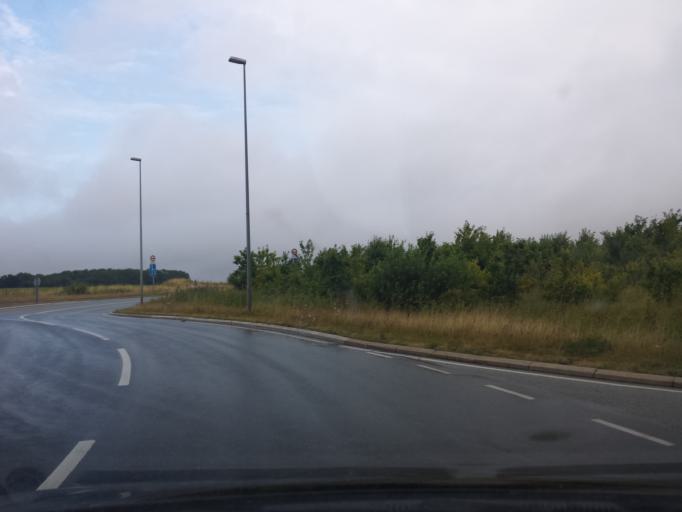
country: DK
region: South Denmark
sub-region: Sonderborg Kommune
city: Augustenborg
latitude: 54.9543
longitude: 9.8997
